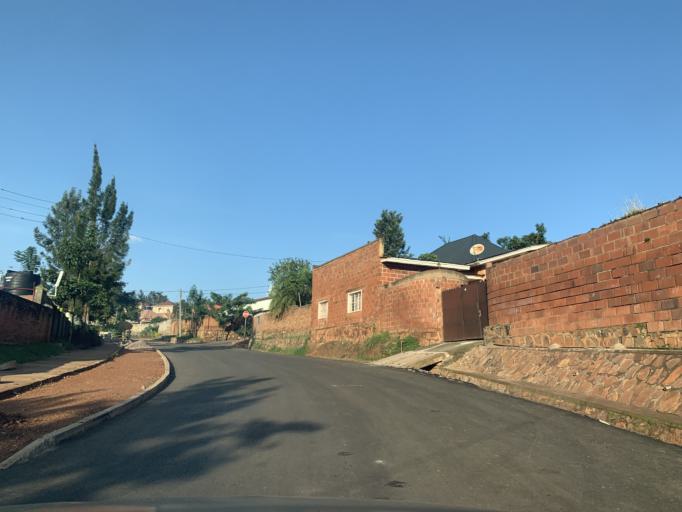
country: RW
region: Kigali
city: Kigali
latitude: -1.9676
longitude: 30.1001
